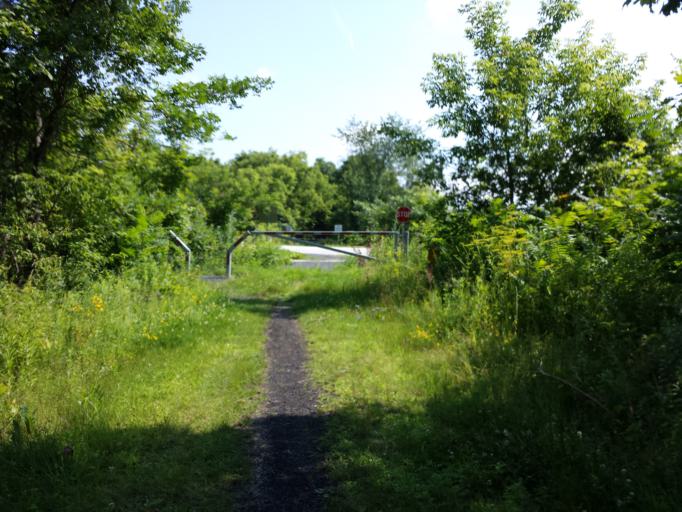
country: US
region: Vermont
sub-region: Rutland County
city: Poultney
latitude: 43.5616
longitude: -73.2249
